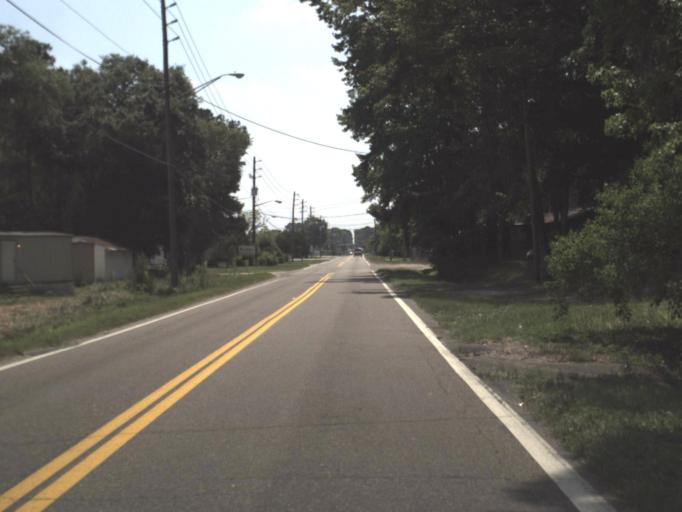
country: US
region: Florida
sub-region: Duval County
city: Jacksonville
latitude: 30.3642
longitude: -81.7374
